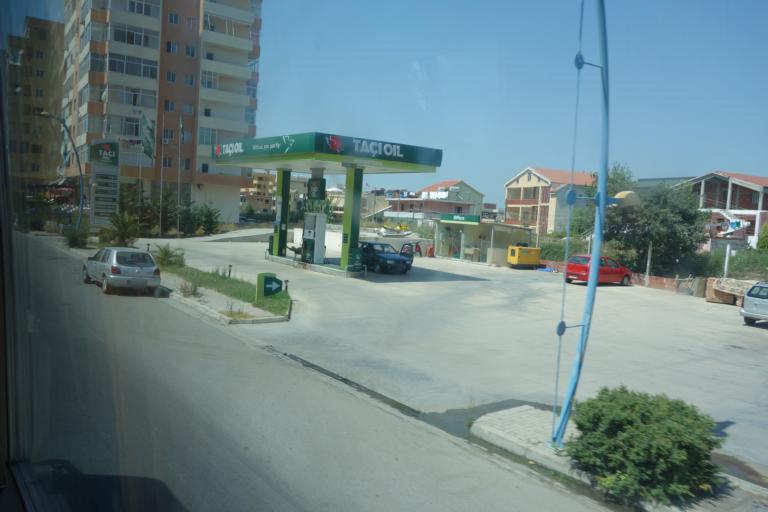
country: AL
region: Durres
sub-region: Rrethi i Durresit
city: Rrashbull
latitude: 41.2990
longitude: 19.5029
